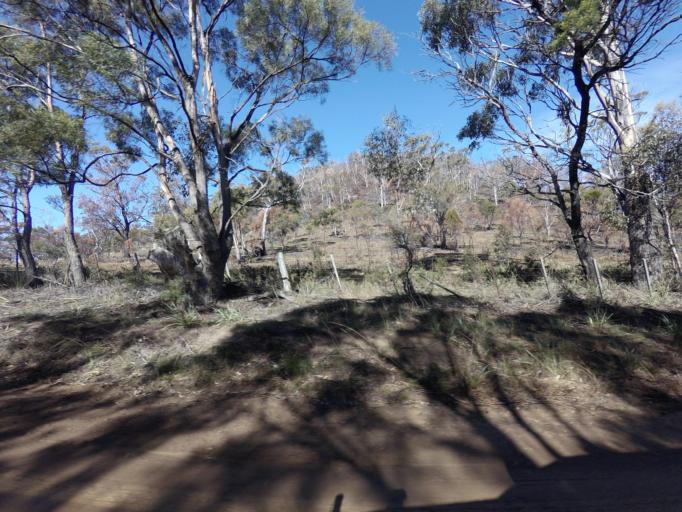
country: AU
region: Tasmania
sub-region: Sorell
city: Sorell
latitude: -42.4139
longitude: 147.9493
